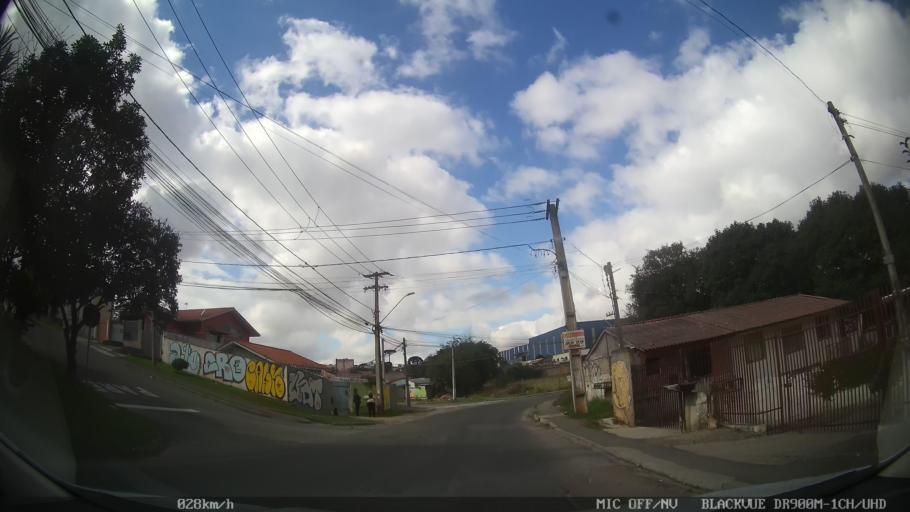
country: BR
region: Parana
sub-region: Colombo
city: Colombo
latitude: -25.3588
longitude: -49.2097
